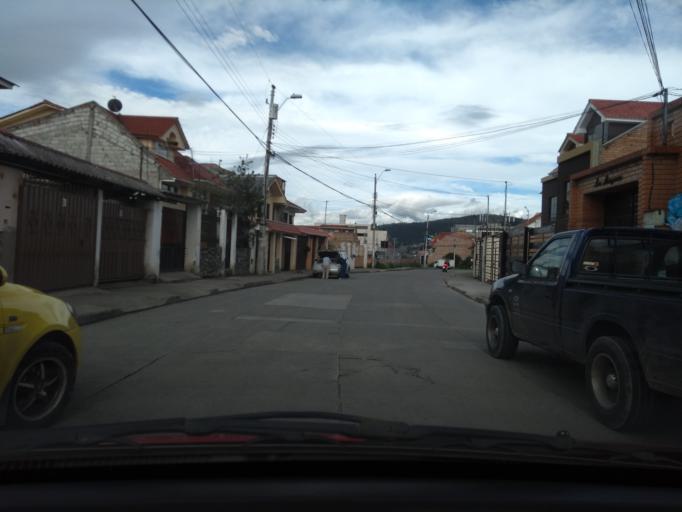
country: EC
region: Azuay
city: Cuenca
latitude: -2.9086
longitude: -79.0247
